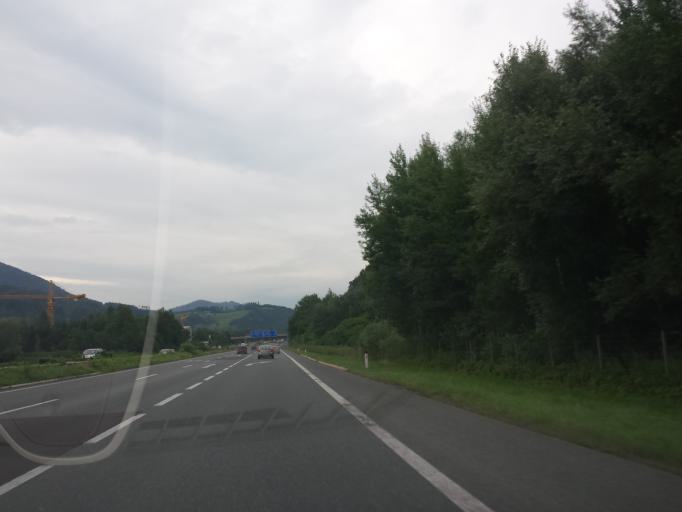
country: AT
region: Styria
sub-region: Politischer Bezirk Graz-Umgebung
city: Deutschfeistritz
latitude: 47.1726
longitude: 15.3324
